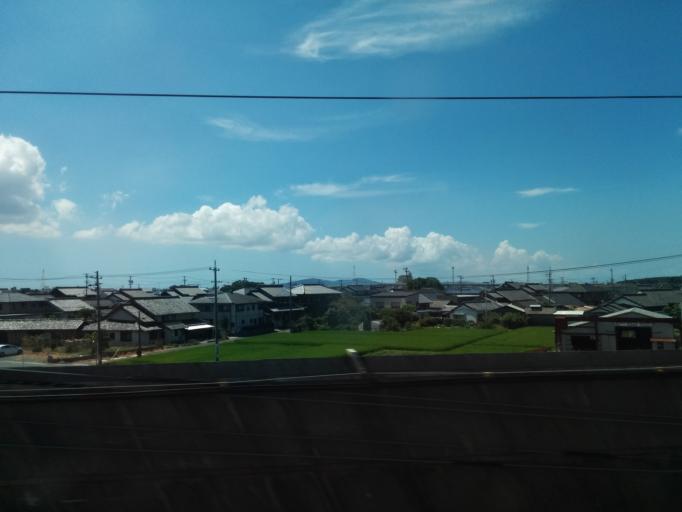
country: JP
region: Aichi
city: Kozakai-cho
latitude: 34.7937
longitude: 137.3395
